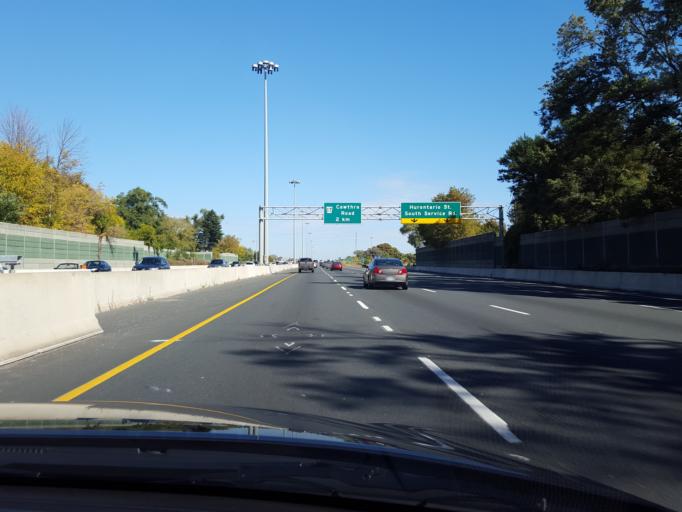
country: CA
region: Ontario
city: Mississauga
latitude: 43.5643
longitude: -79.6040
